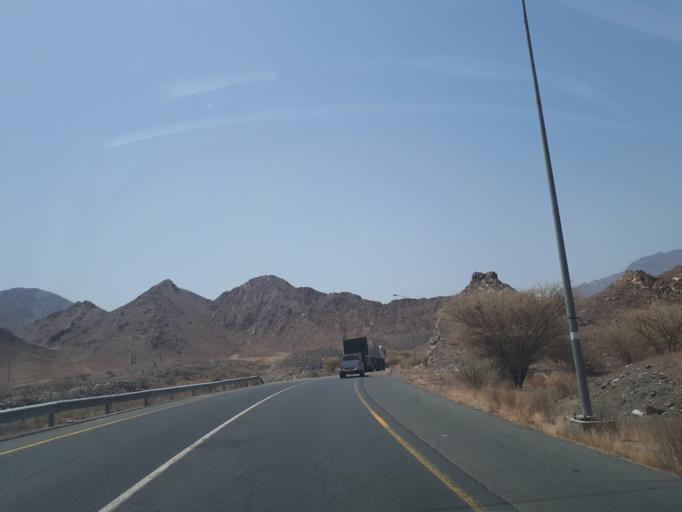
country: OM
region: Muhafazat ad Dakhiliyah
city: Sufalat Sama'il
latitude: 23.2267
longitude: 58.0797
